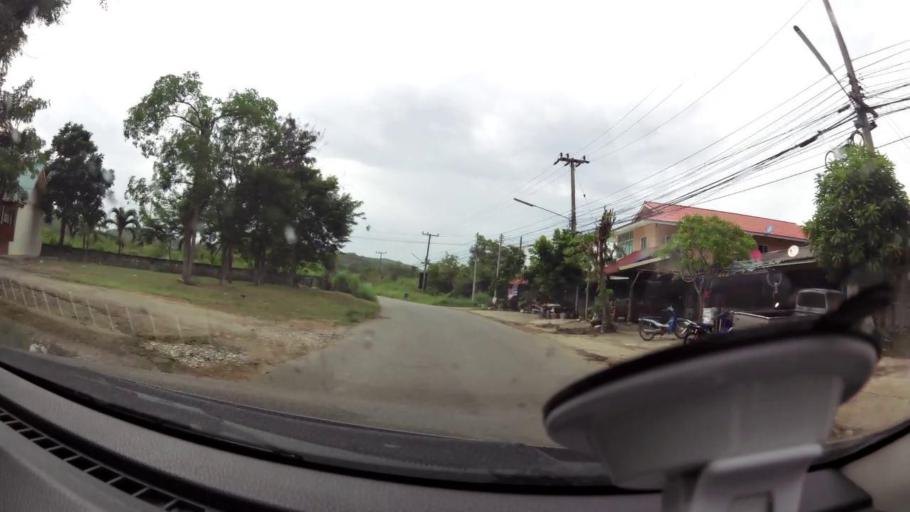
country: TH
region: Prachuap Khiri Khan
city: Pran Buri
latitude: 12.4451
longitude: 99.9672
